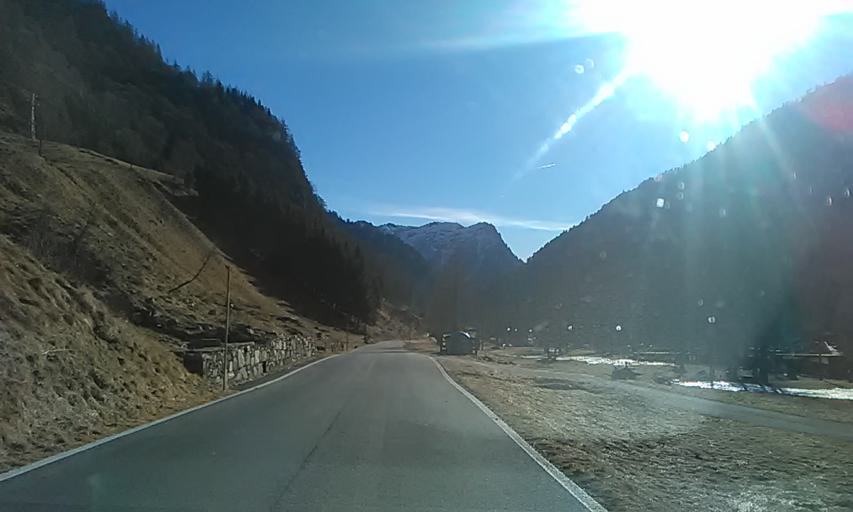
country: IT
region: Piedmont
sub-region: Provincia di Vercelli
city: Carcoforo
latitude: 45.9066
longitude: 8.0523
